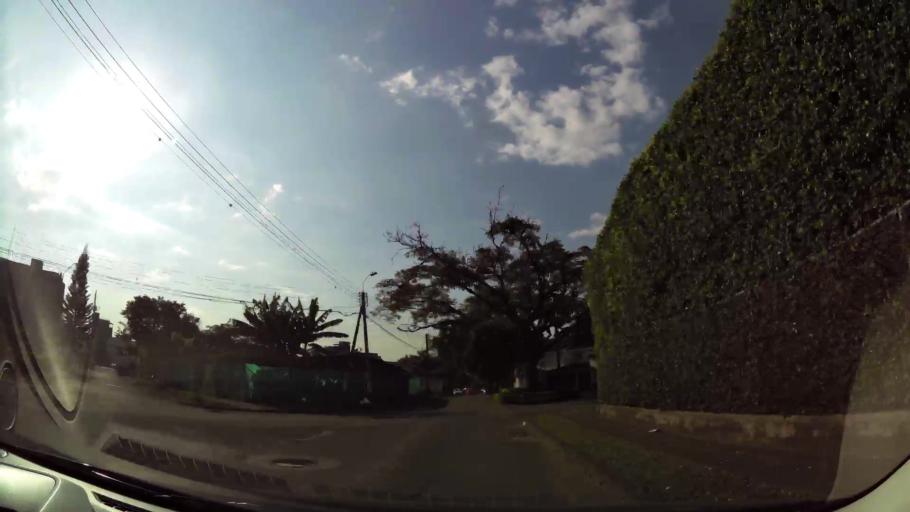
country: CO
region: Valle del Cauca
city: Cali
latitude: 3.4180
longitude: -76.5413
